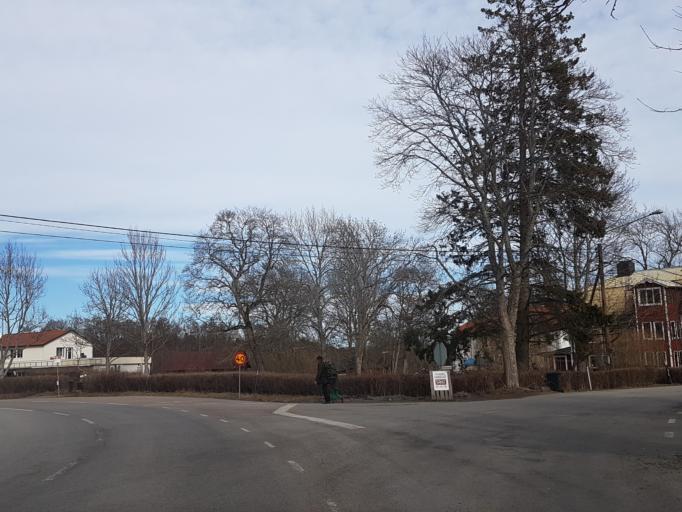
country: SE
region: Stockholm
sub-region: Norrtalje Kommun
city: Bjorko
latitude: 59.6614
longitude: 18.9140
